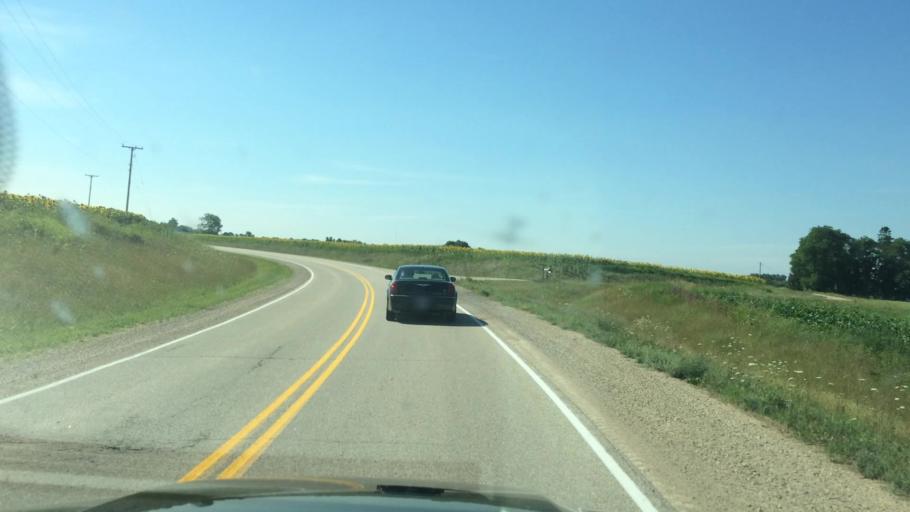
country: US
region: Wisconsin
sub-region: Shawano County
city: Bonduel
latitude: 44.7893
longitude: -88.3526
